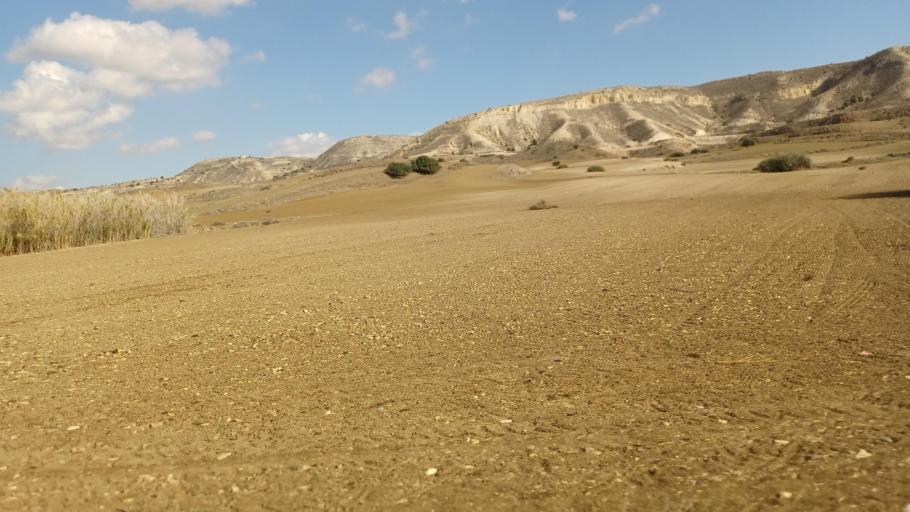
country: CY
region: Larnaka
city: Voroklini
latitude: 35.0177
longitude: 33.6447
